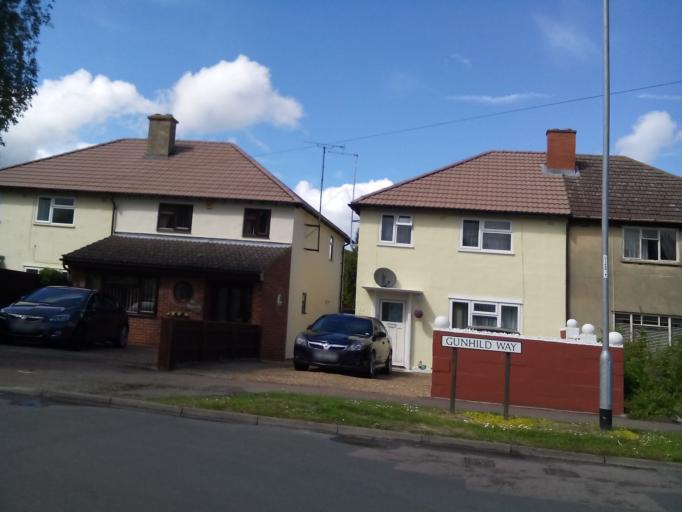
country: GB
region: England
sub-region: Cambridgeshire
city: Cambridge
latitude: 52.1837
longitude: 0.1584
